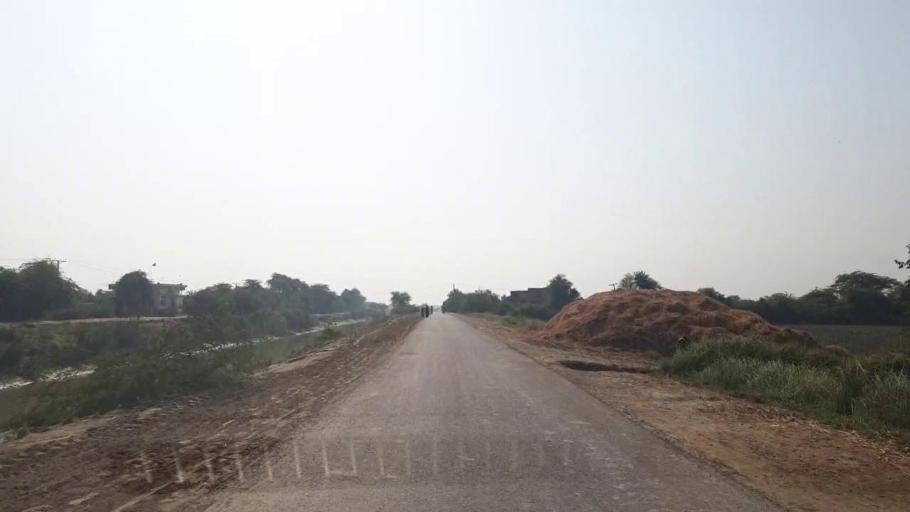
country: PK
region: Sindh
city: Matli
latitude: 24.9680
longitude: 68.5992
